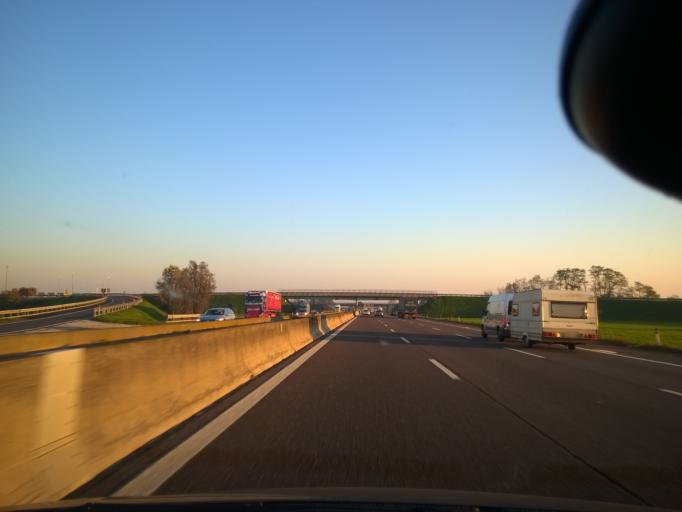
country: IT
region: Lombardy
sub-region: Citta metropolitana di Milano
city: Melegnano
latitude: 45.3583
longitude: 9.2993
